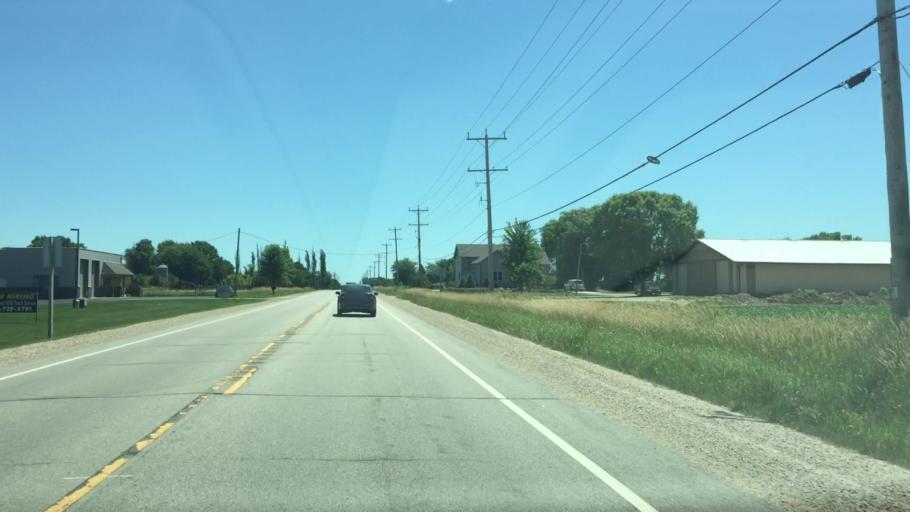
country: US
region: Wisconsin
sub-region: Calumet County
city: Sherwood
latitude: 44.1992
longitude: -88.3195
